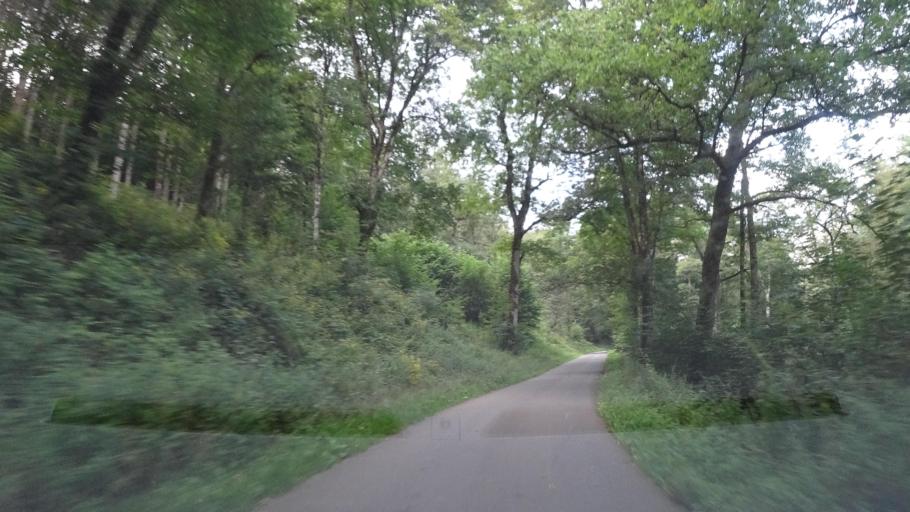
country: BE
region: Wallonia
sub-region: Province du Luxembourg
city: Herbeumont
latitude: 49.7751
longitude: 5.2553
